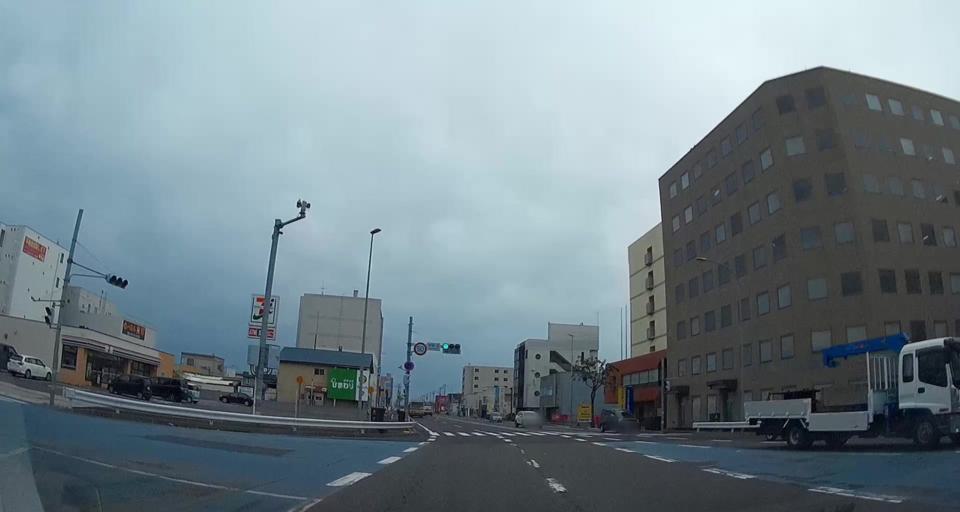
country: JP
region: Hokkaido
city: Tomakomai
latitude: 42.6325
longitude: 141.6008
